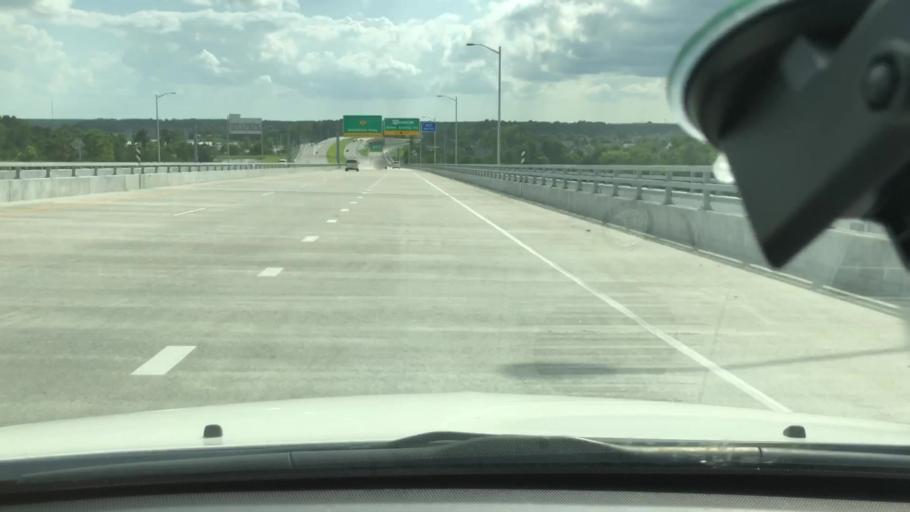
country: US
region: Virginia
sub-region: City of Chesapeake
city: Chesapeake
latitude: 36.7346
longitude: -76.2965
